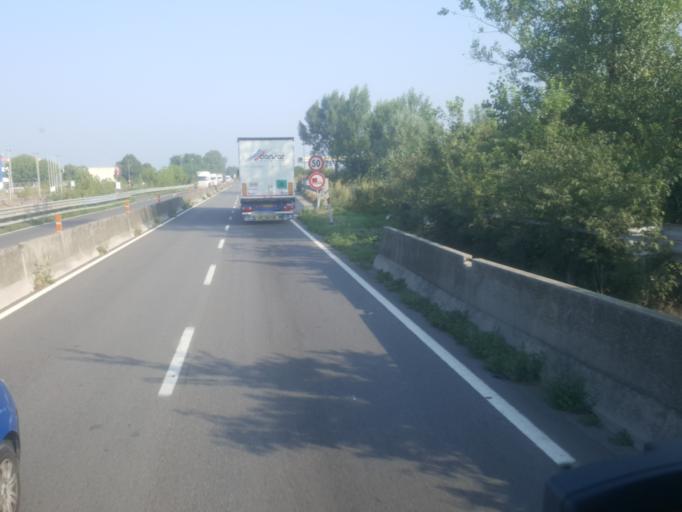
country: IT
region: Emilia-Romagna
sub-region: Provincia di Ravenna
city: Ravenna
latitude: 44.4135
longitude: 12.1707
